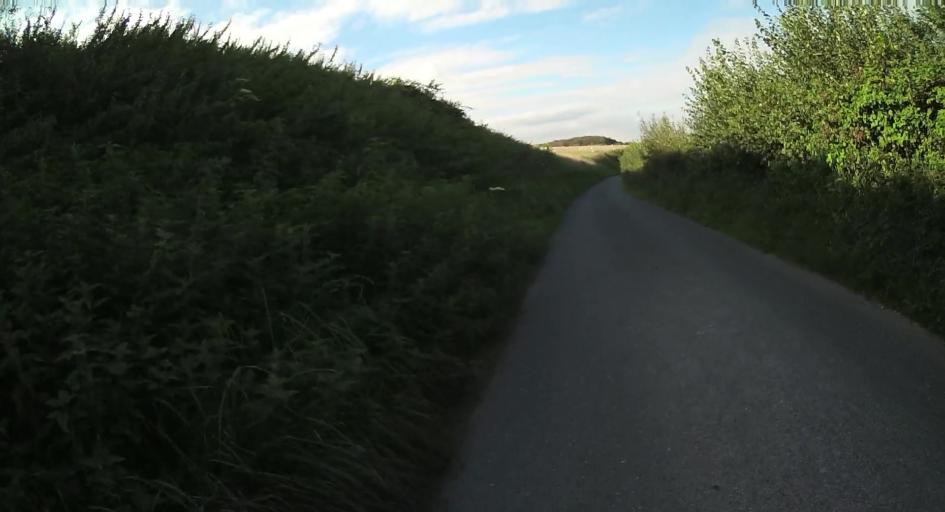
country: GB
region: England
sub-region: Isle of Wight
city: Newport
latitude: 50.6527
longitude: -1.3025
